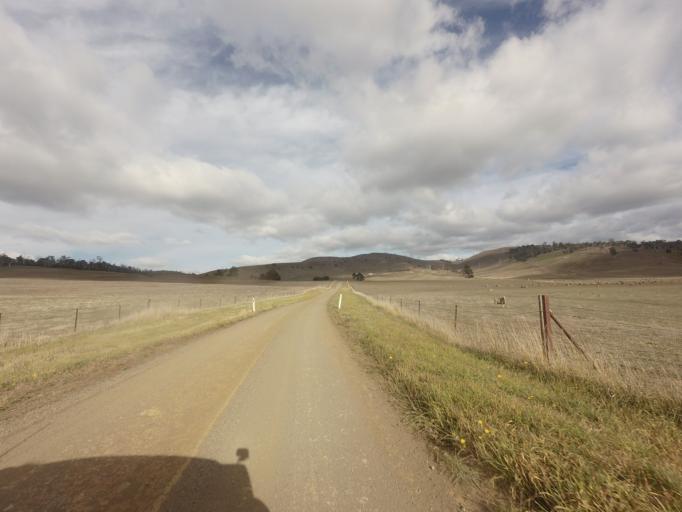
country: AU
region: Tasmania
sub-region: Brighton
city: Bridgewater
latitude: -42.4657
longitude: 147.2790
